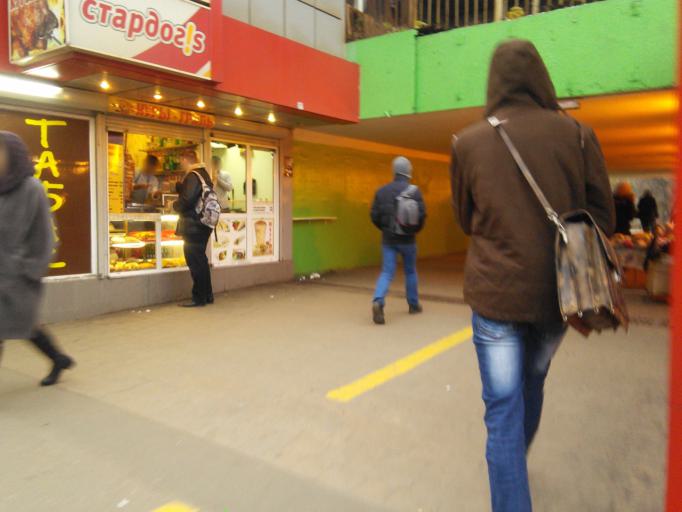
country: RU
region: Moscow
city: Mar'ina Roshcha
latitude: 55.8080
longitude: 37.5803
